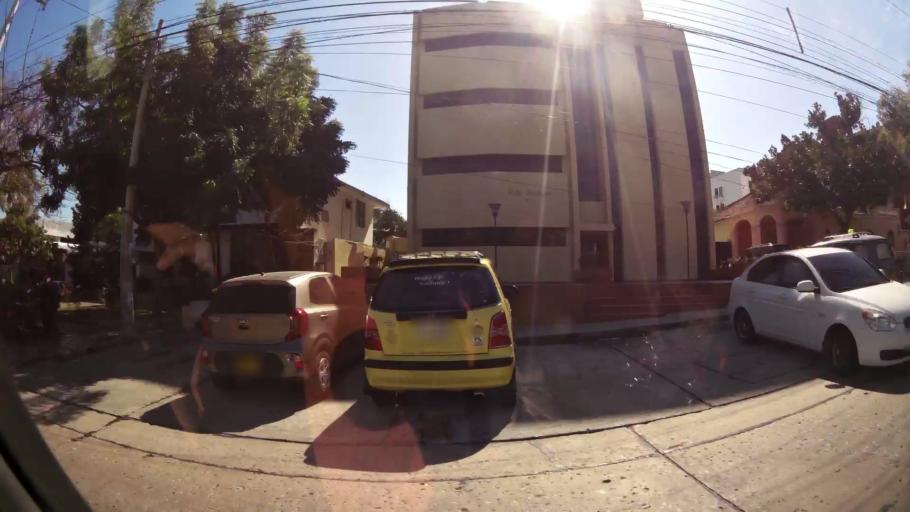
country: CO
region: Atlantico
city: Barranquilla
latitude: 10.9962
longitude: -74.7958
